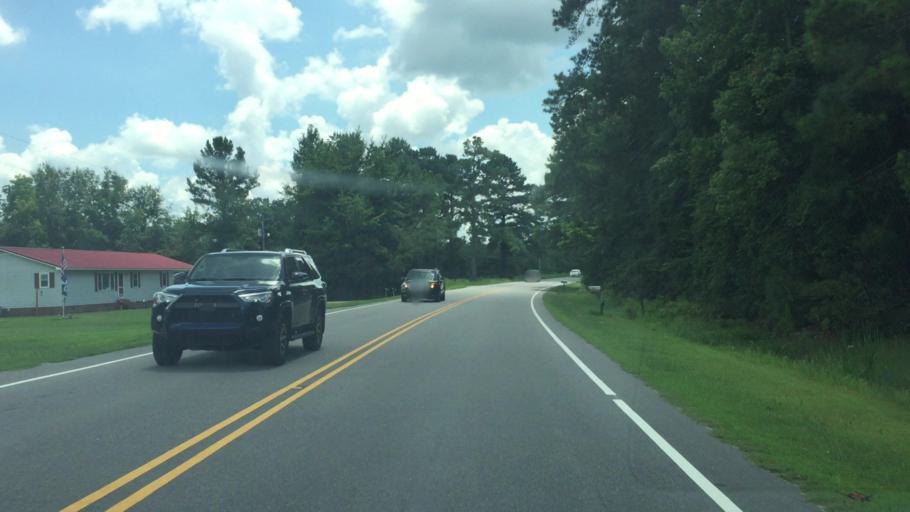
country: US
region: North Carolina
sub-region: Columbus County
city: Chadbourn
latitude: 34.2737
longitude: -78.8129
